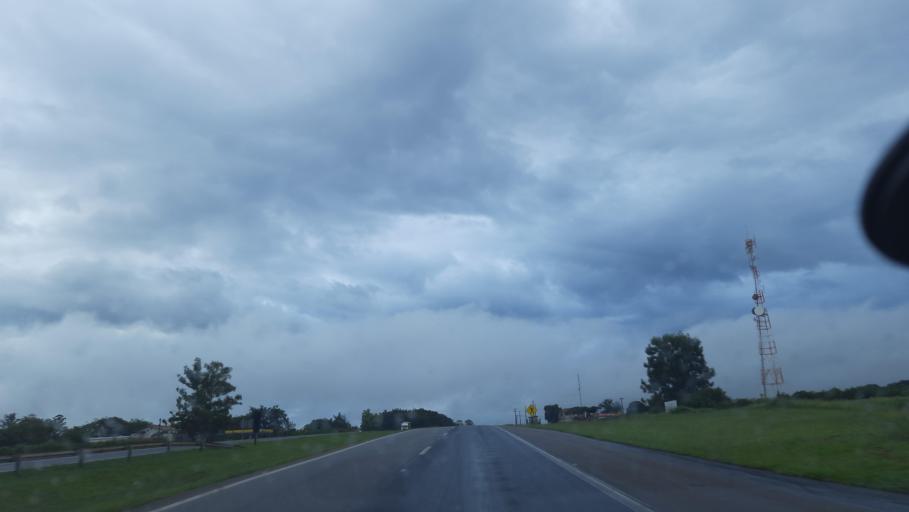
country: BR
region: Sao Paulo
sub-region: Moji-Guacu
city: Mogi-Gaucu
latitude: -22.2212
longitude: -46.9797
